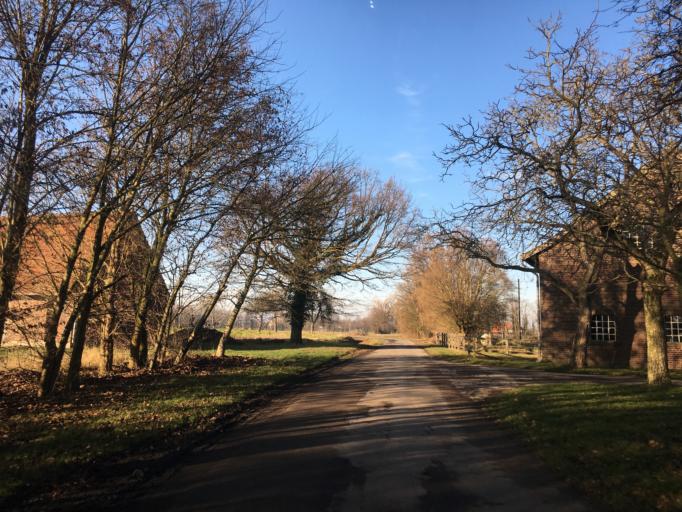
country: DE
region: North Rhine-Westphalia
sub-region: Regierungsbezirk Munster
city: Altenberge
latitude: 52.0351
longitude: 7.5304
